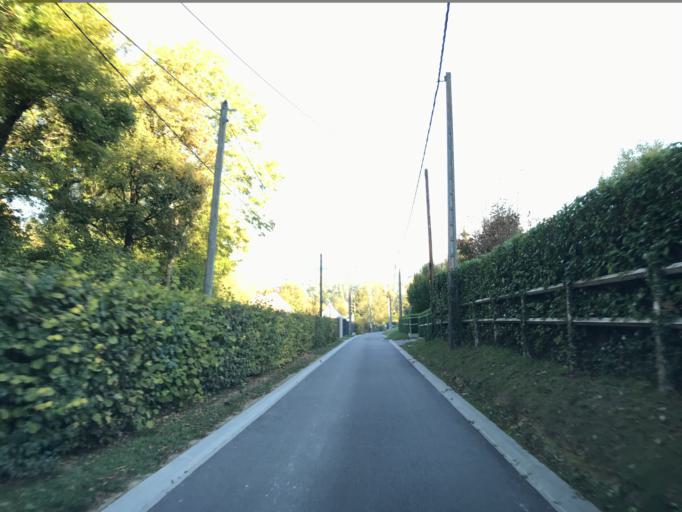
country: FR
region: Haute-Normandie
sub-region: Departement de l'Eure
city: Houlbec-Cocherel
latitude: 49.0730
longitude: 1.2756
